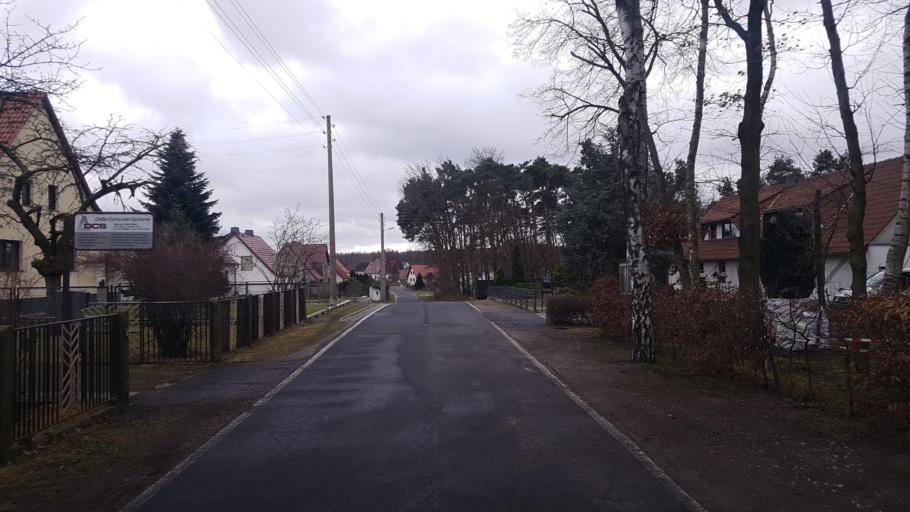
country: DE
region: Brandenburg
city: Kroppen
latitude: 51.3646
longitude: 13.7888
